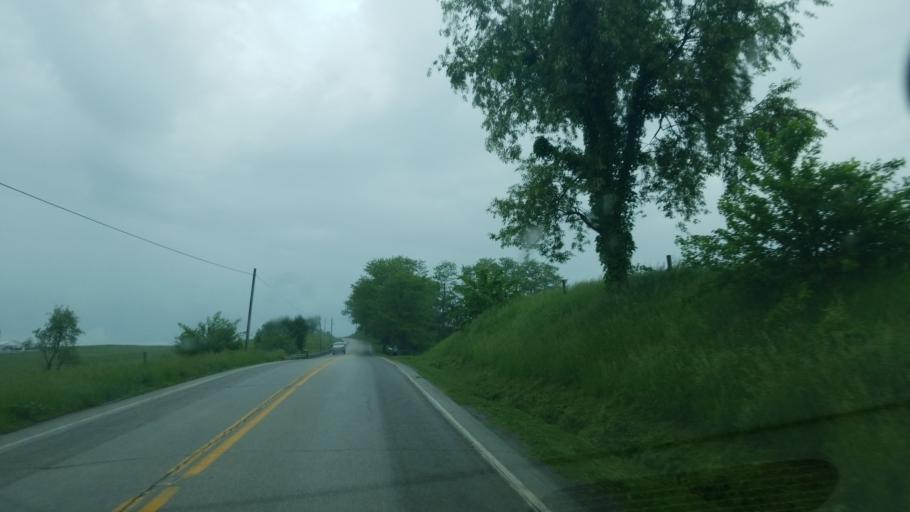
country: US
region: Ohio
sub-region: Tuscarawas County
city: Sugarcreek
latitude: 40.4932
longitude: -81.7589
